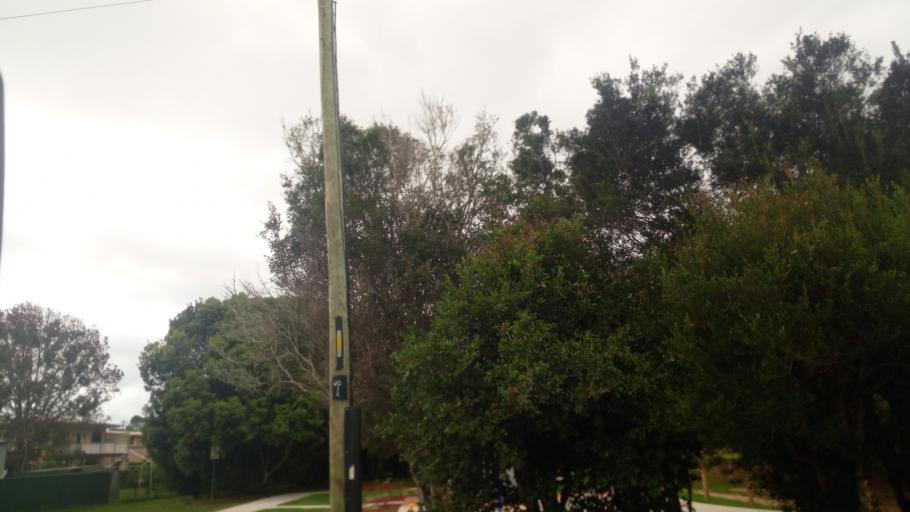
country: AU
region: Queensland
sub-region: Tablelands
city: Tolga
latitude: -17.2162
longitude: 145.5437
